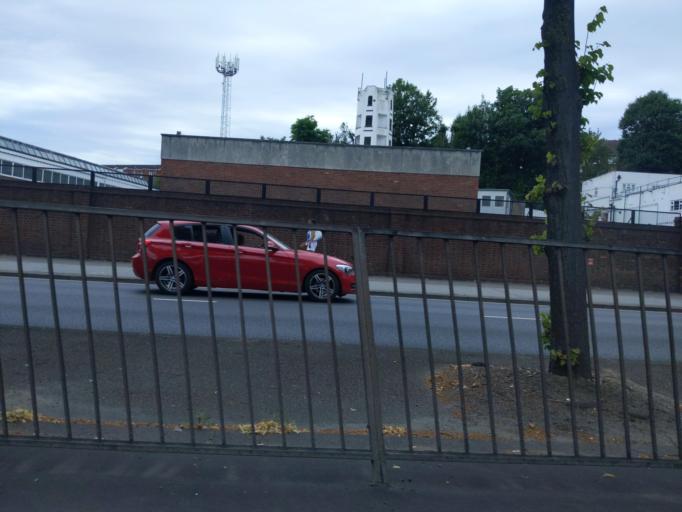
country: GB
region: England
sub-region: Greater London
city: South Croydon
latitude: 51.3695
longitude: -0.1050
